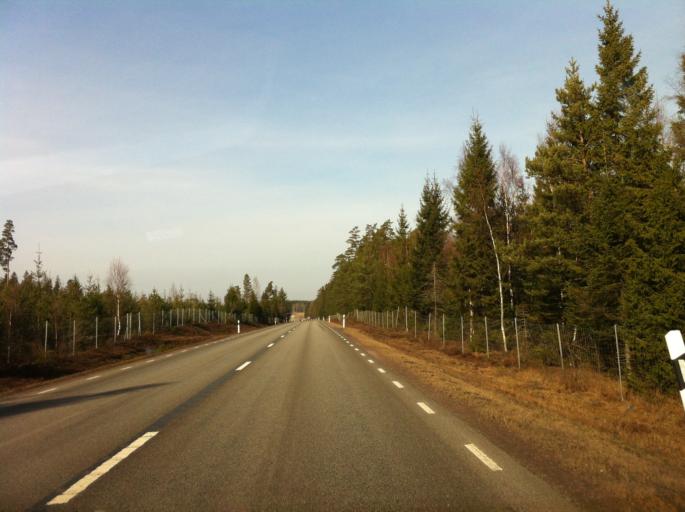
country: SE
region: Vaestra Goetaland
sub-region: Tidaholms Kommun
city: Tidaholm
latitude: 58.1835
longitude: 13.8988
